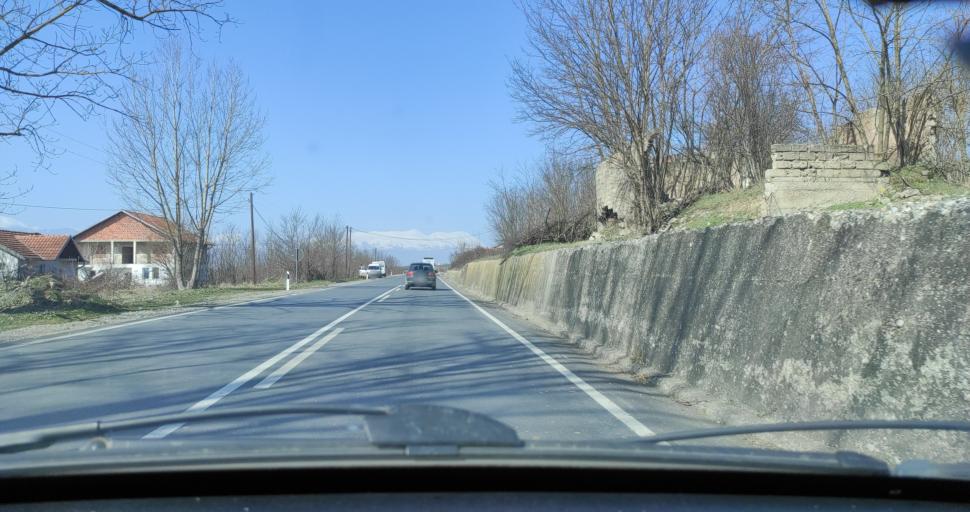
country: XK
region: Pec
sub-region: Komuna e Klines
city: Klina
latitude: 42.6012
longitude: 20.5244
